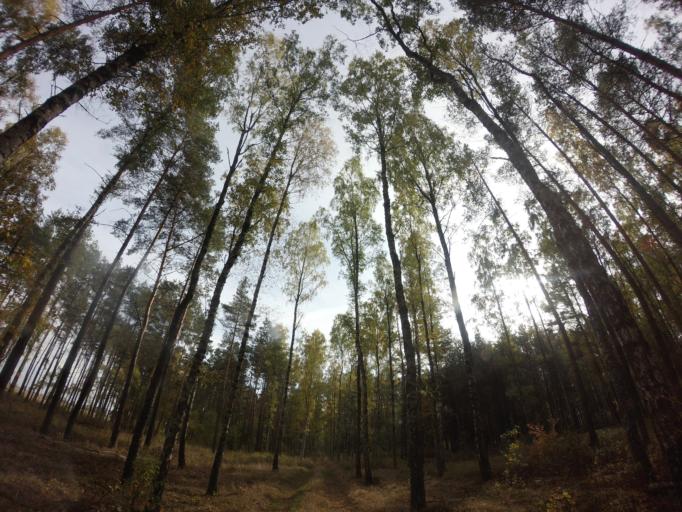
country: PL
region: West Pomeranian Voivodeship
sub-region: Powiat choszczenski
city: Drawno
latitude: 53.2488
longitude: 15.6804
